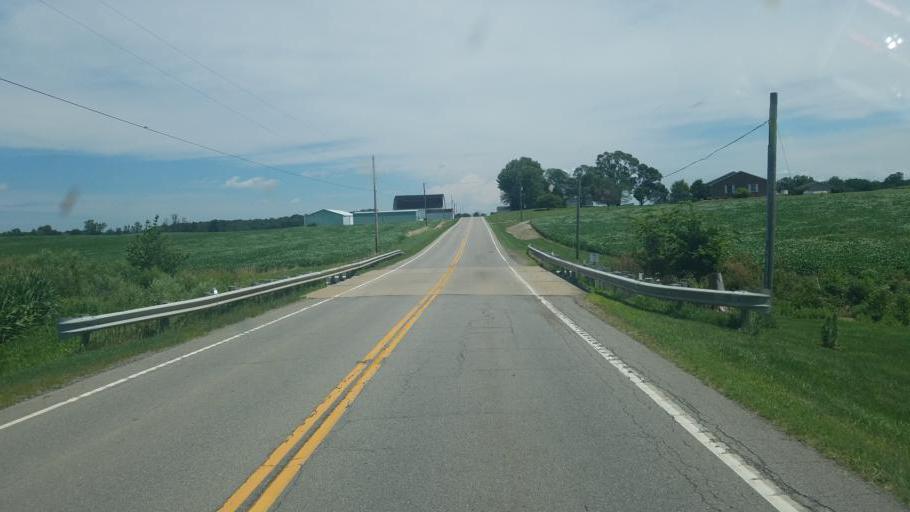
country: US
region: Ohio
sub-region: Richland County
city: Shelby
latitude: 40.8884
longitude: -82.5852
